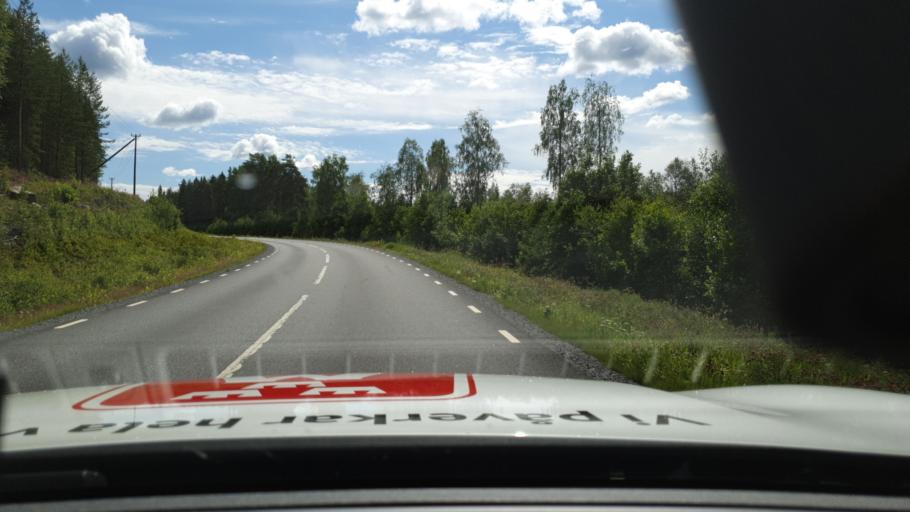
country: SE
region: Norrbotten
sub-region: Bodens Kommun
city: Saevast
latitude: 65.8234
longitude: 21.8890
